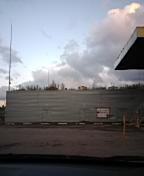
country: RU
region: Moskovskaya
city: Zhukovskiy
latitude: 55.5092
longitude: 38.1355
